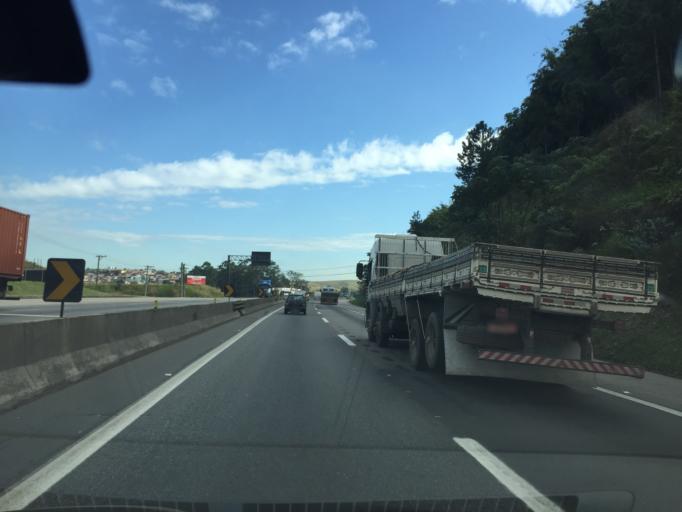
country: BR
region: Sao Paulo
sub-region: Jacarei
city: Jacarei
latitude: -23.2989
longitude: -46.0117
